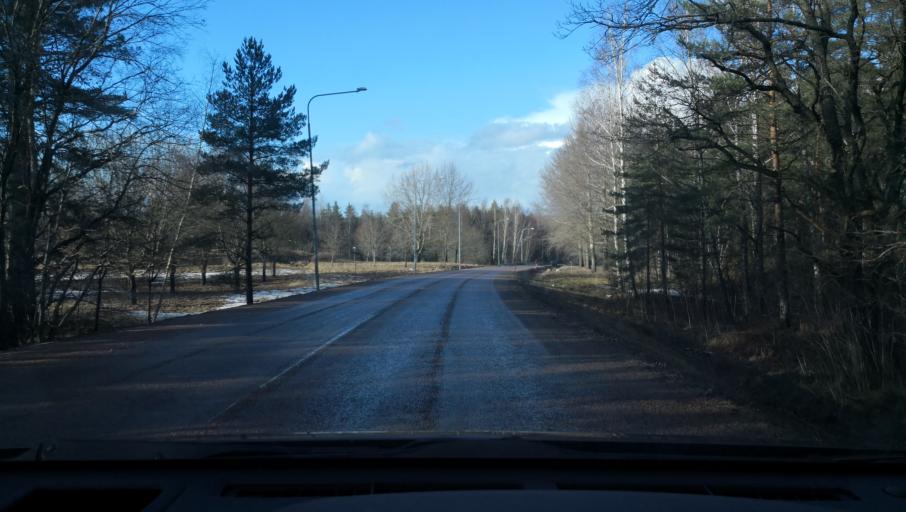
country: SE
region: Vaestmanland
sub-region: Arboga Kommun
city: Arboga
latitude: 59.3803
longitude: 15.8393
